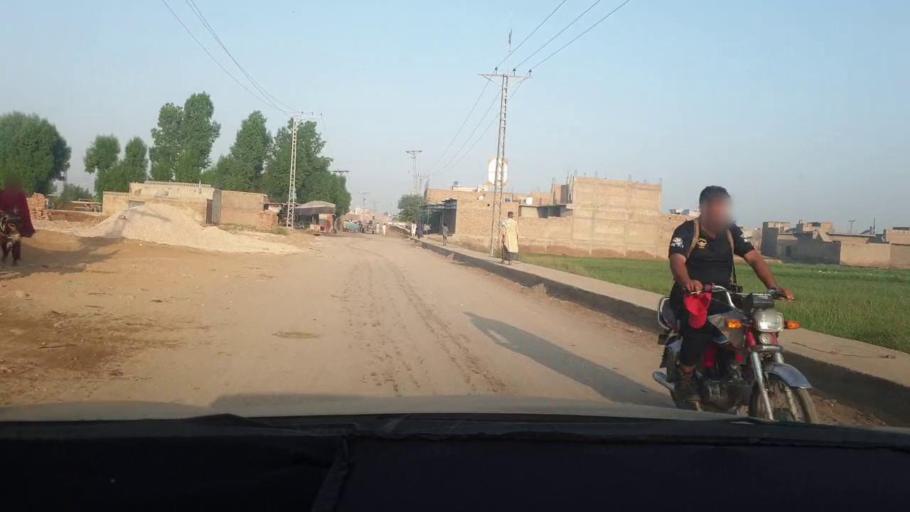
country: PK
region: Sindh
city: Larkana
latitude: 27.5412
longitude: 68.2187
